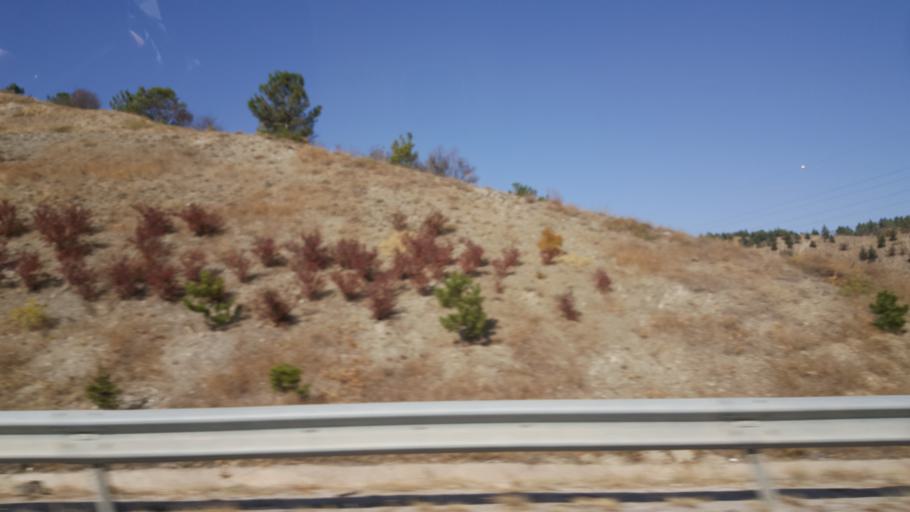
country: TR
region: Ankara
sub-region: Goelbasi
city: Golbasi
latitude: 39.8142
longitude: 32.8112
